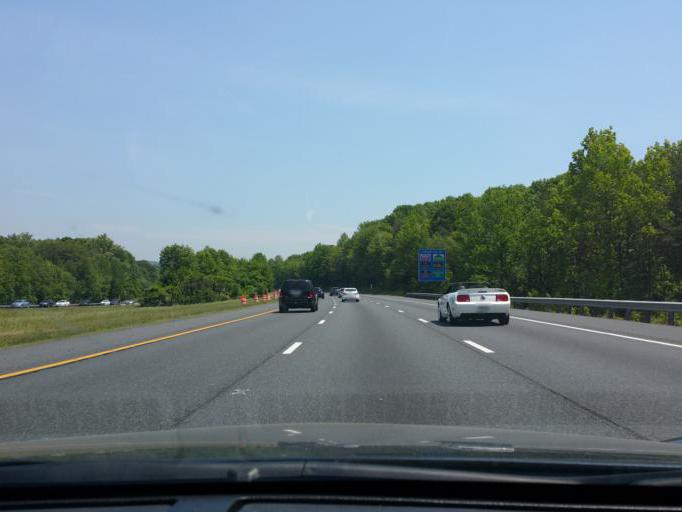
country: US
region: Maryland
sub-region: Harford County
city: Riverside
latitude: 39.4694
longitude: -76.2793
